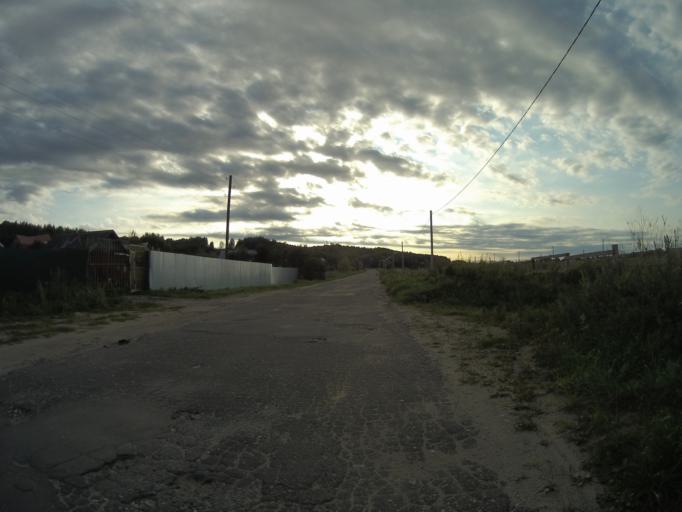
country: RU
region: Vladimir
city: Raduzhnyy
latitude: 56.0173
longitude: 40.3463
